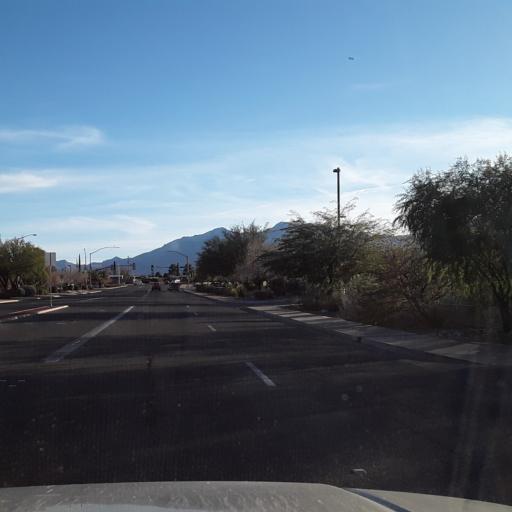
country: US
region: Arizona
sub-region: Cochise County
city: Sierra Vista
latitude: 31.5539
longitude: -110.2777
